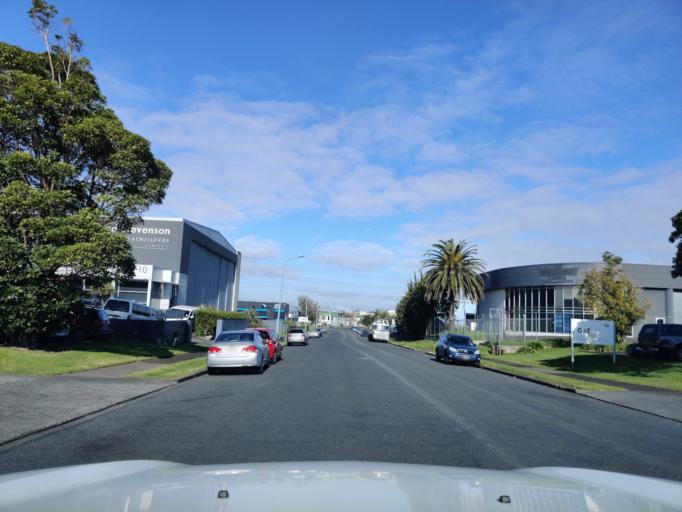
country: NZ
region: Auckland
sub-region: Auckland
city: Manukau City
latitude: -36.9392
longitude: 174.8821
